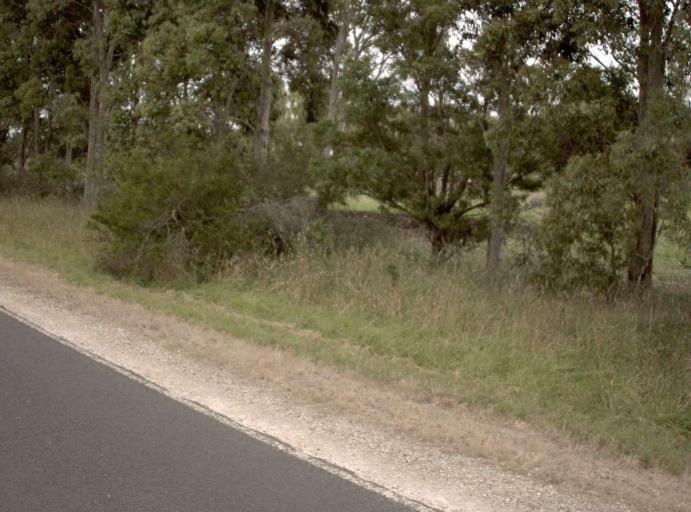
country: AU
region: Victoria
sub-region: Wellington
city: Sale
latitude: -38.0465
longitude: 146.9464
